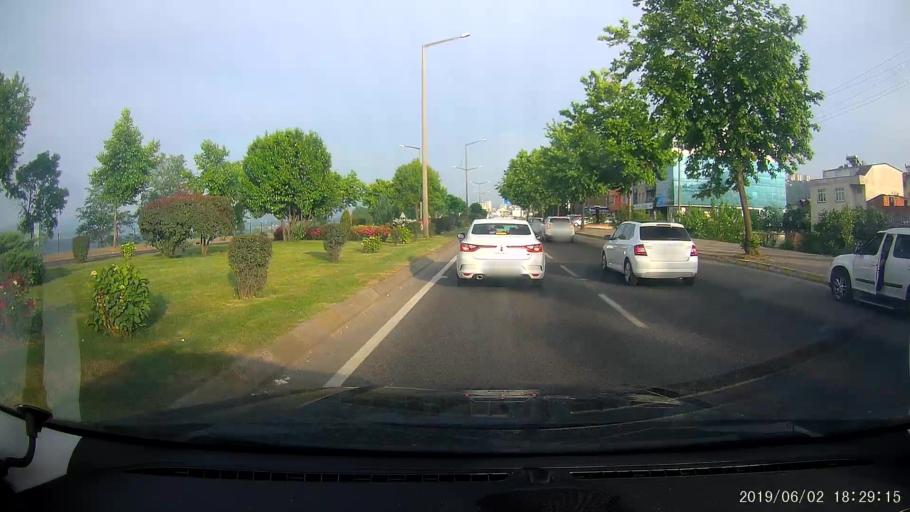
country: TR
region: Ordu
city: Fatsa
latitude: 41.0393
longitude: 37.4900
